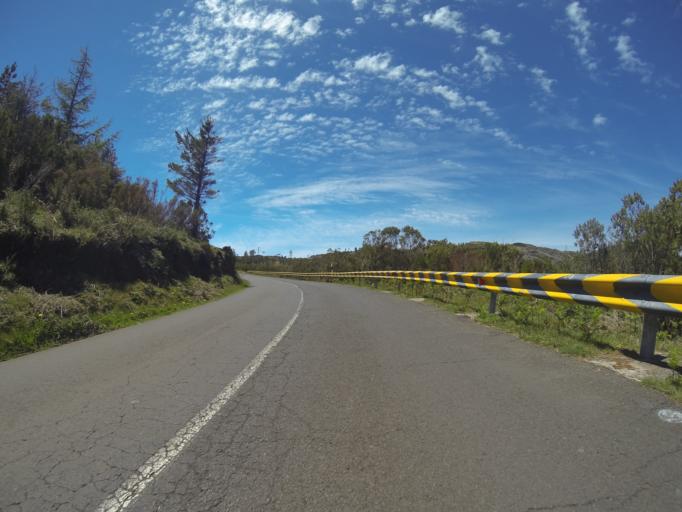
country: PT
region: Madeira
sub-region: Funchal
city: Nossa Senhora do Monte
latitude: 32.7135
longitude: -16.8993
